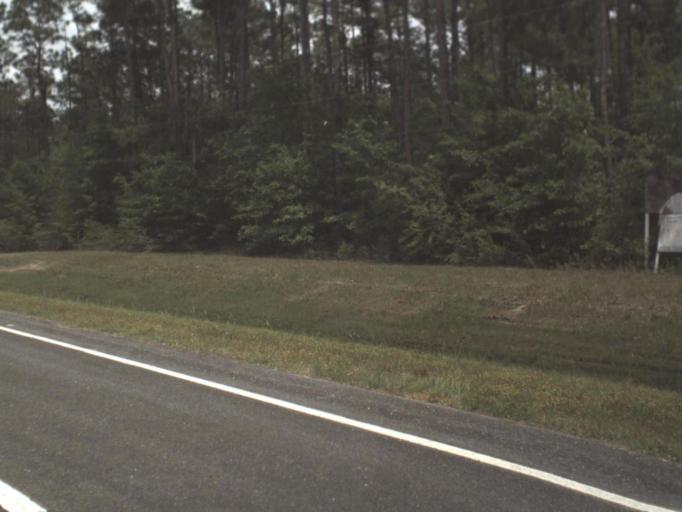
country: US
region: Florida
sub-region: Santa Rosa County
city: Bagdad
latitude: 30.5293
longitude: -87.0872
